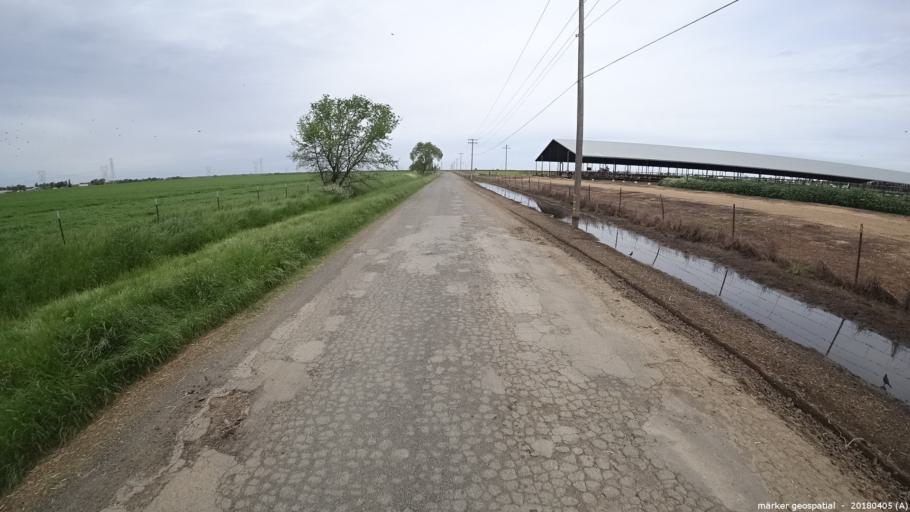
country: US
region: California
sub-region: Sacramento County
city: Galt
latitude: 38.2843
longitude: -121.3513
